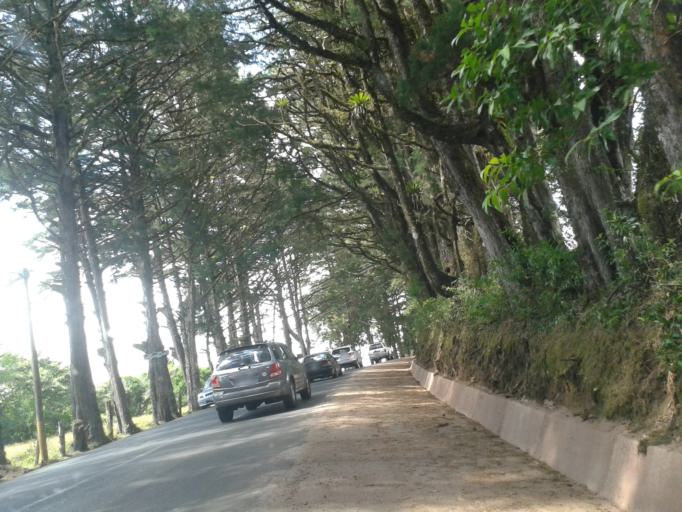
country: CR
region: Alajuela
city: Sabanilla
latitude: 10.1340
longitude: -84.1908
